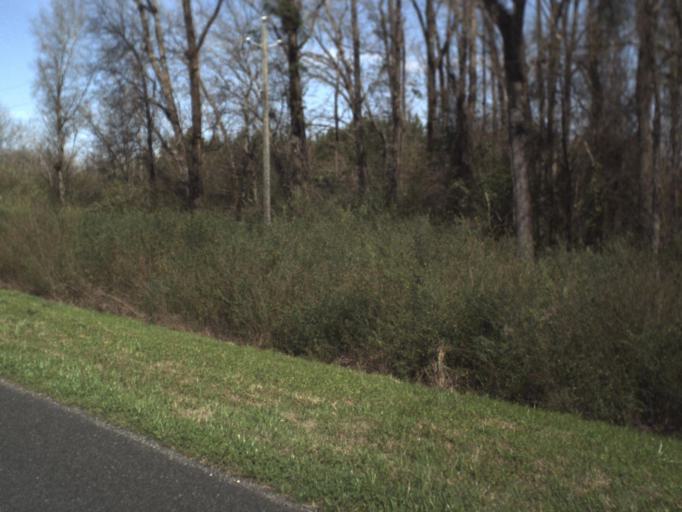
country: US
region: Florida
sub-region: Jackson County
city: Graceville
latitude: 30.9706
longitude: -85.4087
